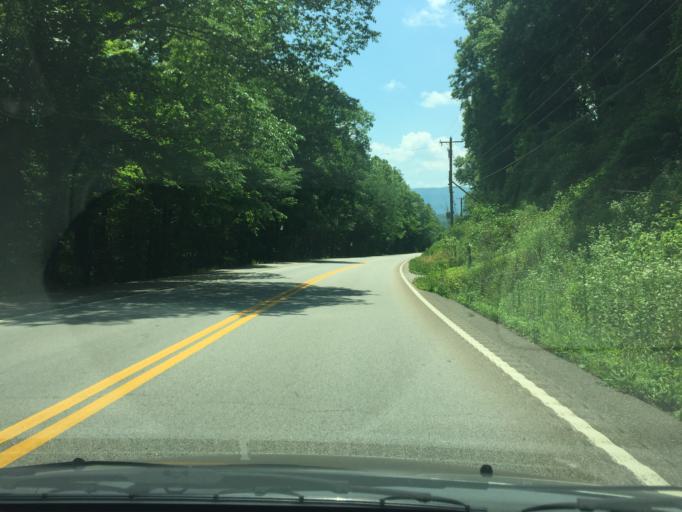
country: US
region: Tennessee
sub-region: Hamilton County
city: Lookout Mountain
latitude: 35.0330
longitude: -85.4079
